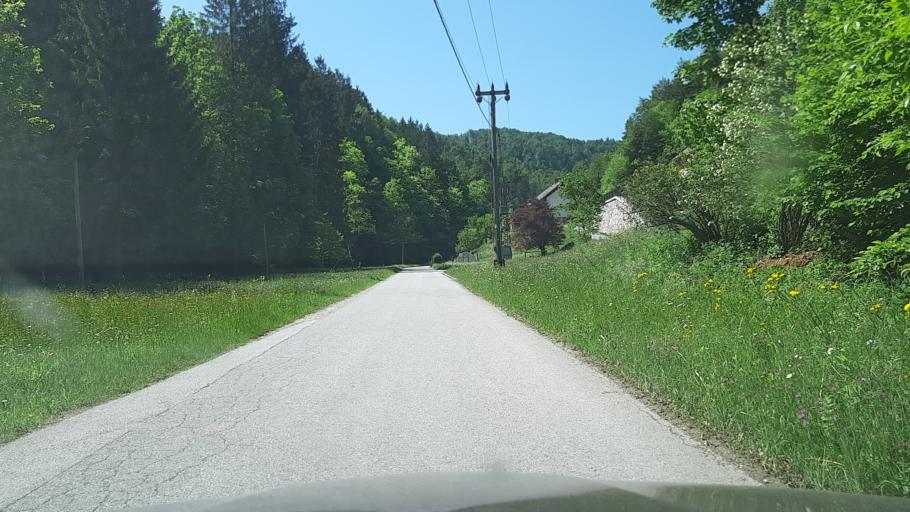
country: SI
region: Skofja Loka
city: Skofja Loka
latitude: 46.1345
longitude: 14.2941
